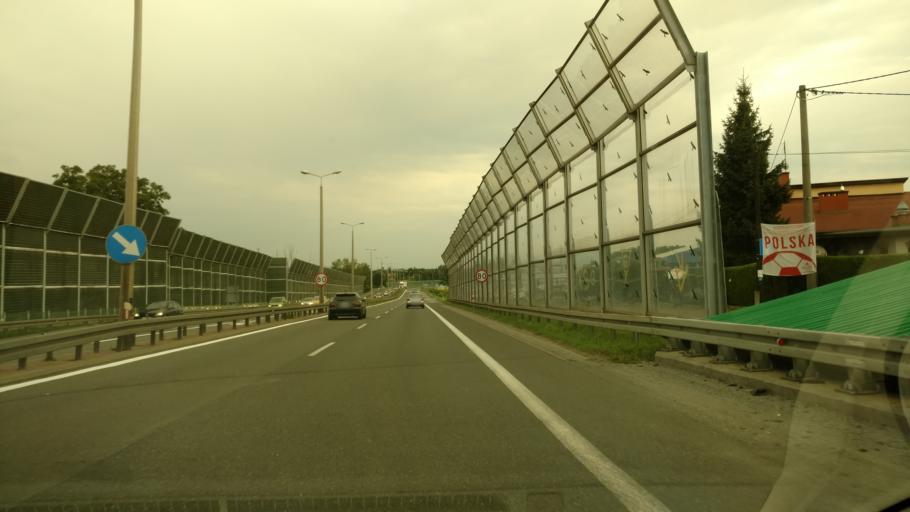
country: PL
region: Silesian Voivodeship
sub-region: Powiat pszczynski
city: Pszczyna
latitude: 49.9840
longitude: 18.9566
